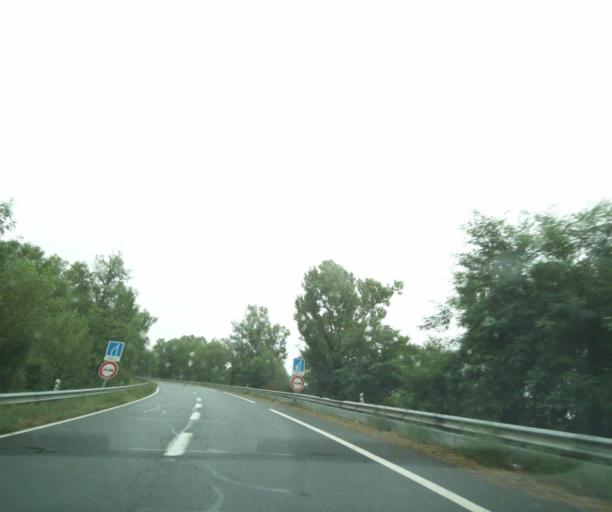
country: FR
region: Midi-Pyrenees
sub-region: Departement du Tarn
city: Arthes
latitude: 43.9615
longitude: 2.1799
